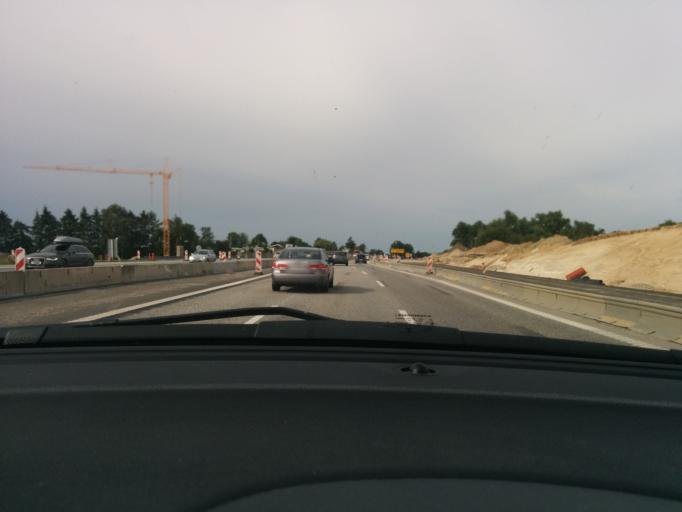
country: DK
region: Zealand
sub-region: Koge Kommune
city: Koge
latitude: 55.4849
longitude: 12.1625
